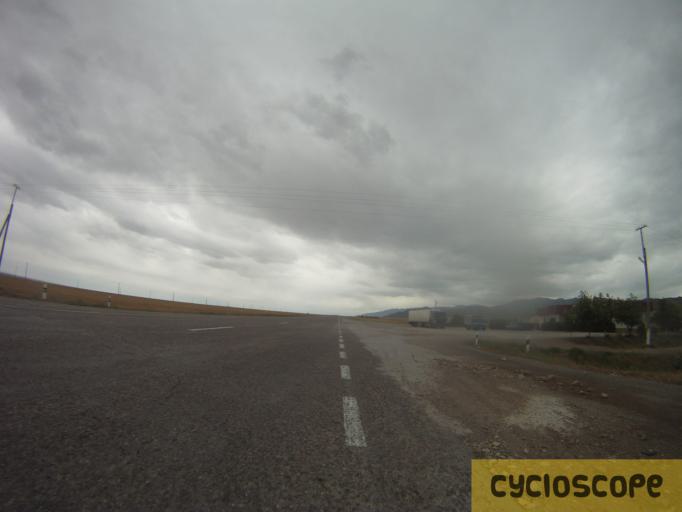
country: KZ
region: Zhambyl
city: Georgiyevka
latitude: 43.3472
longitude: 74.9782
